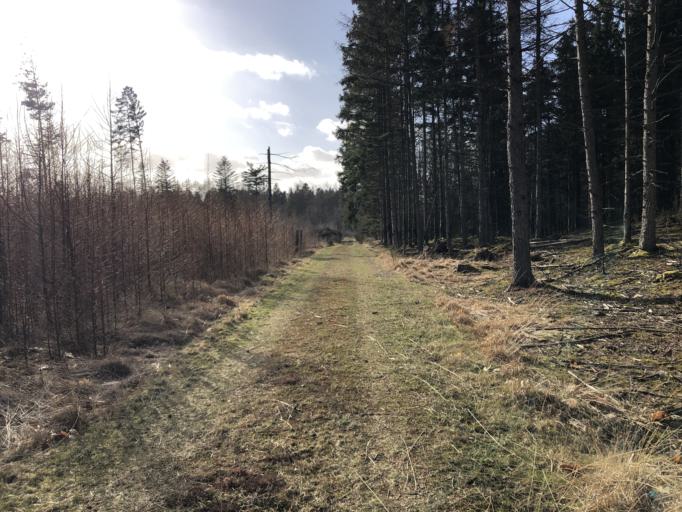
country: DK
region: Central Jutland
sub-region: Holstebro Kommune
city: Ulfborg
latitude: 56.2692
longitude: 8.4395
